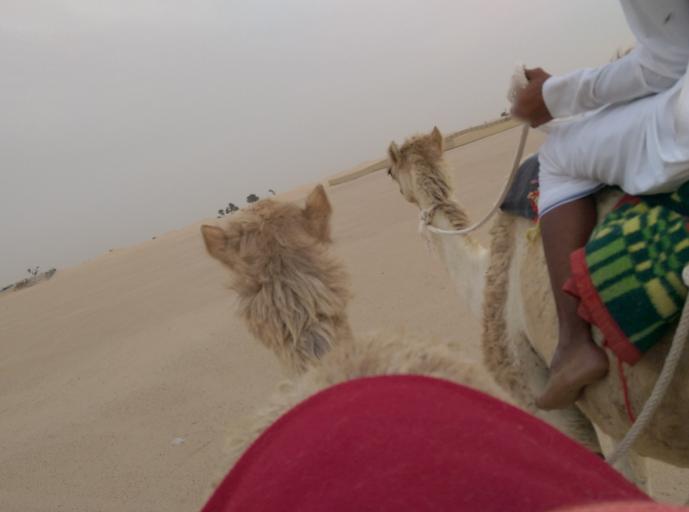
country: AE
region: Dubai
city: Dubai
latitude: 24.9348
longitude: 55.3681
